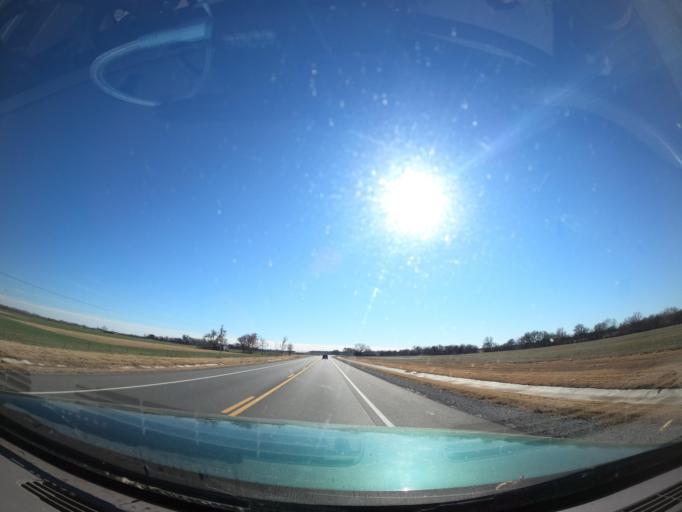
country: US
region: Oklahoma
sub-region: Wagoner County
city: Coweta
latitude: 35.8915
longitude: -95.6592
